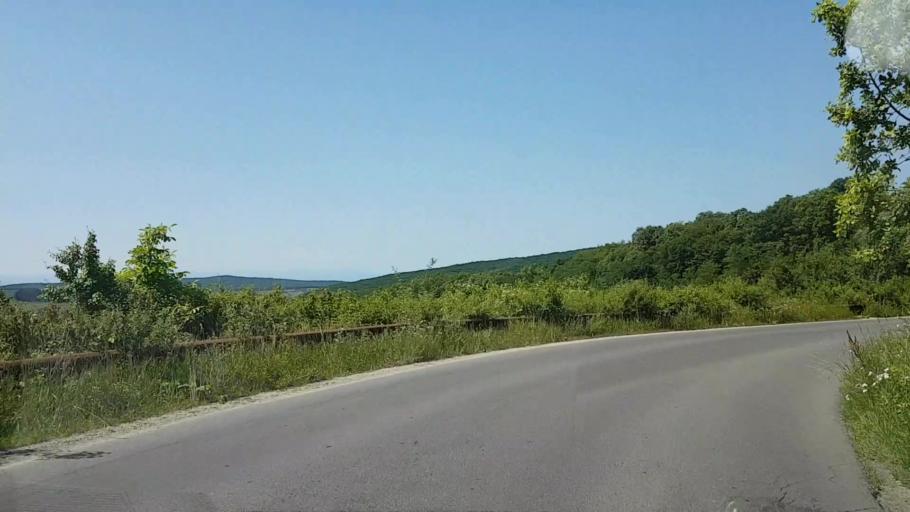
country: RO
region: Sibiu
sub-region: Comuna Bradeni
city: Bradeni
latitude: 46.1031
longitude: 24.8408
